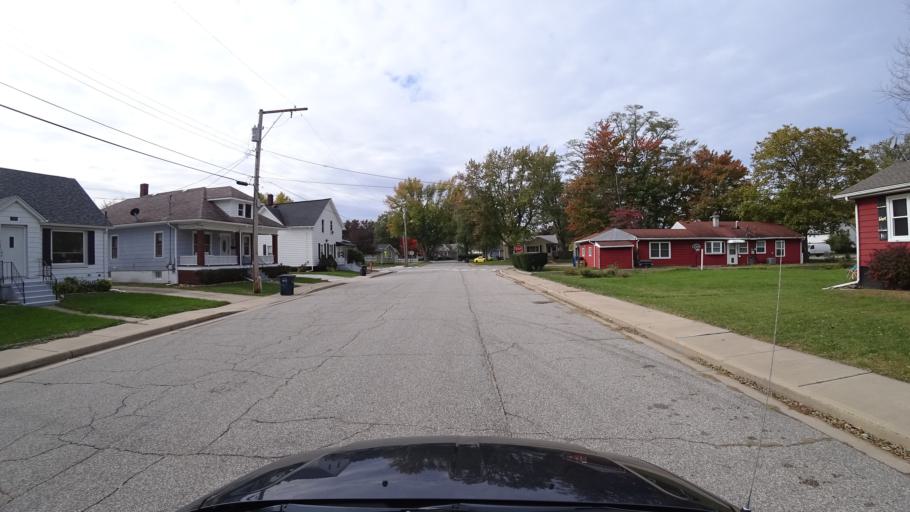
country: US
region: Indiana
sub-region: LaPorte County
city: Michigan City
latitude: 41.7031
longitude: -86.8973
